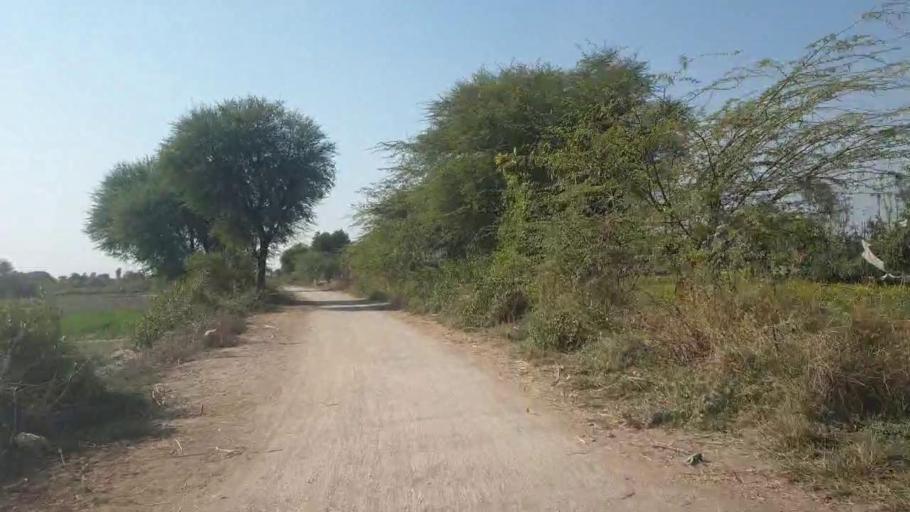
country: PK
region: Sindh
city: Chambar
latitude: 25.3119
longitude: 68.8463
